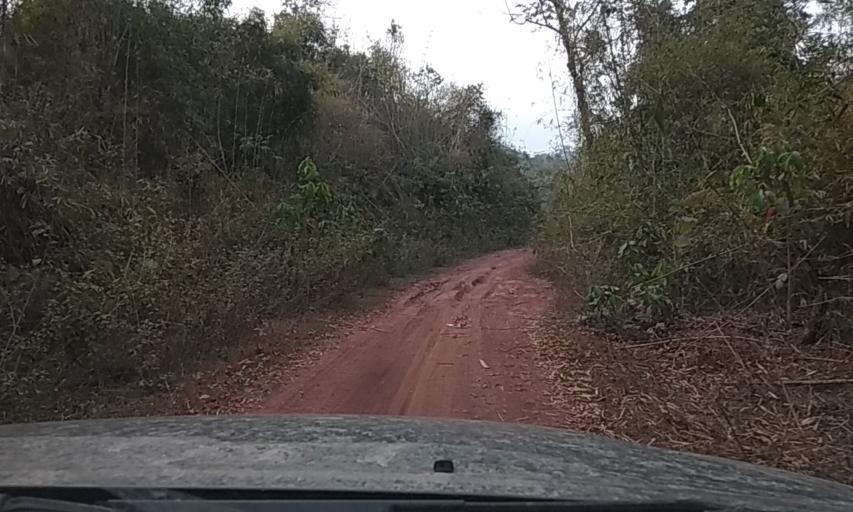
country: TH
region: Nan
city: Mae Charim
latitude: 18.4534
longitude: 101.1958
